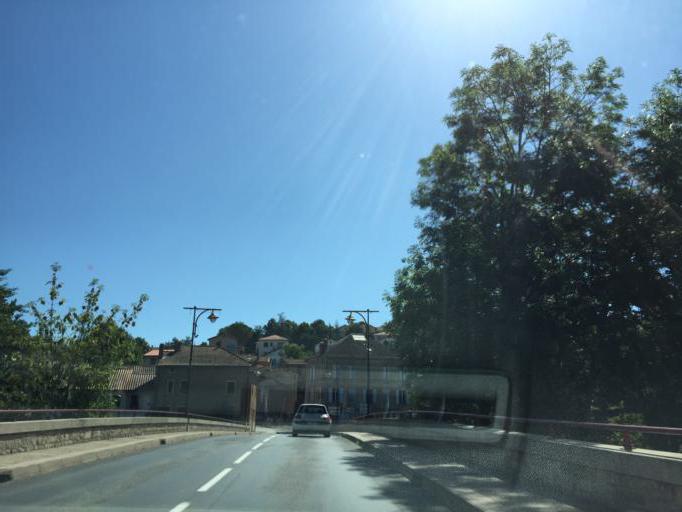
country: FR
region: Midi-Pyrenees
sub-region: Departement de l'Aveyron
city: Saint-Georges-de-Luzencon
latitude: 44.0119
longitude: 2.9651
